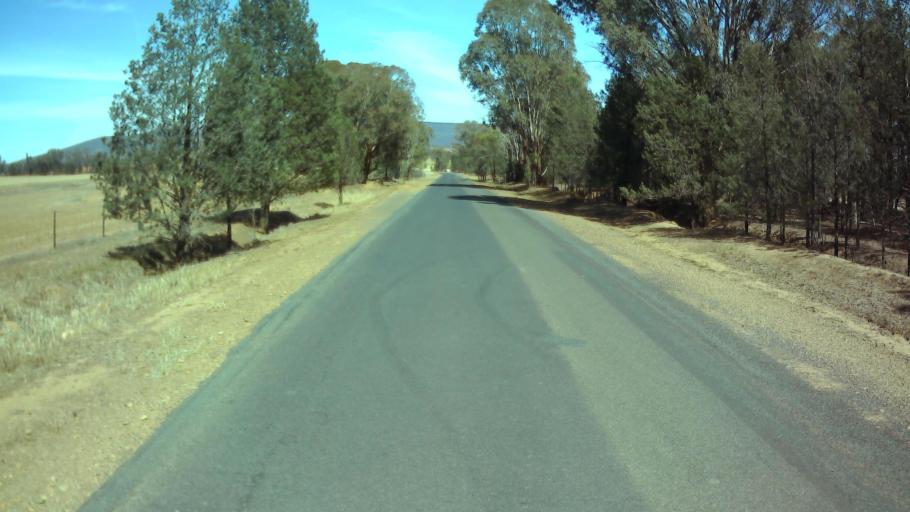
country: AU
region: New South Wales
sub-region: Weddin
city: Grenfell
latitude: -33.9316
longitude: 148.0904
